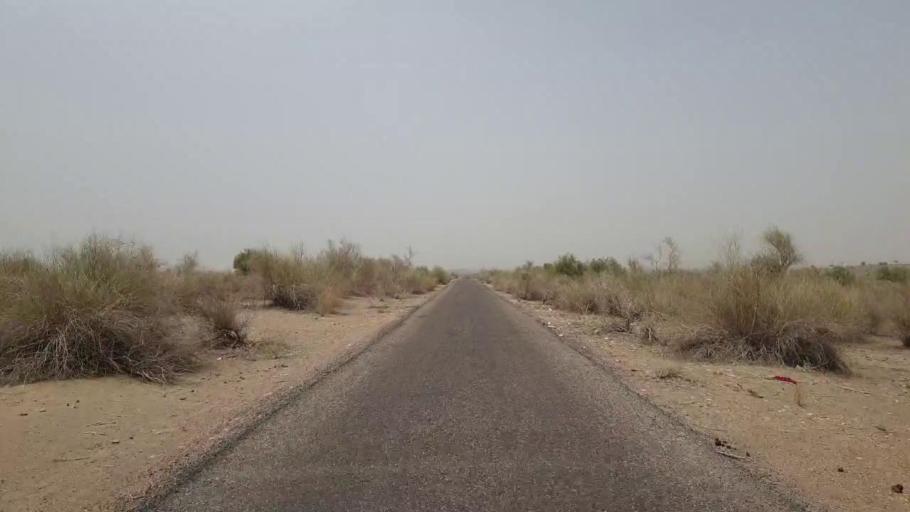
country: PK
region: Sindh
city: Islamkot
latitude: 24.7691
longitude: 70.4859
